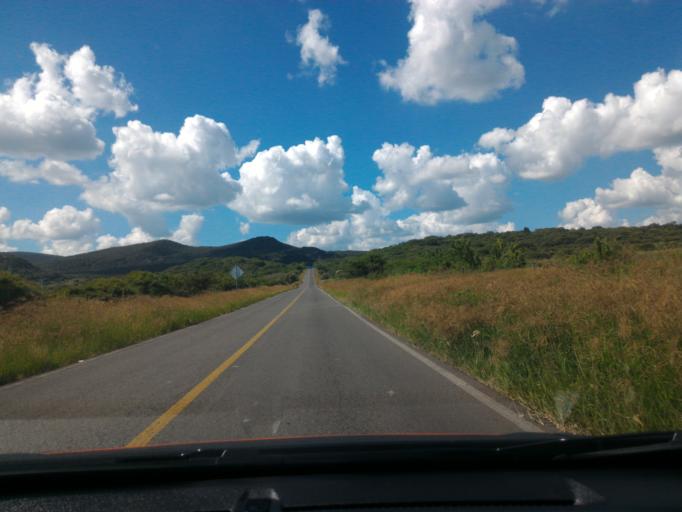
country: MX
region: Guanajuato
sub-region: Penjamo
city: Estacion la Piedad
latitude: 20.5382
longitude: -101.9730
